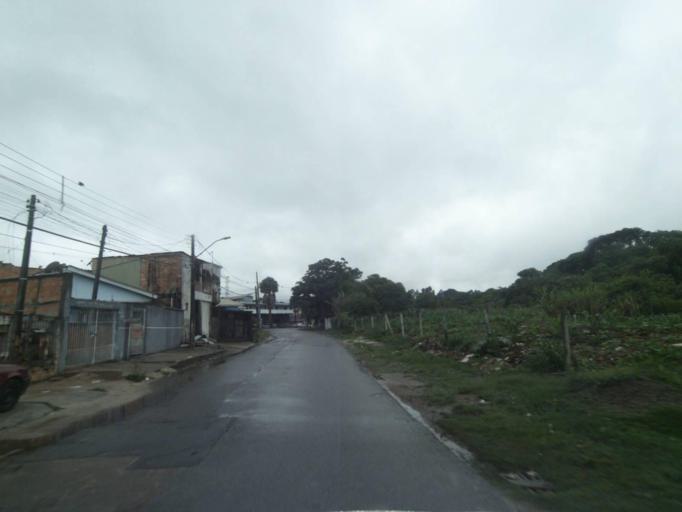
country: BR
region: Parana
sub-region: Araucaria
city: Araucaria
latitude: -25.5339
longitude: -49.3345
